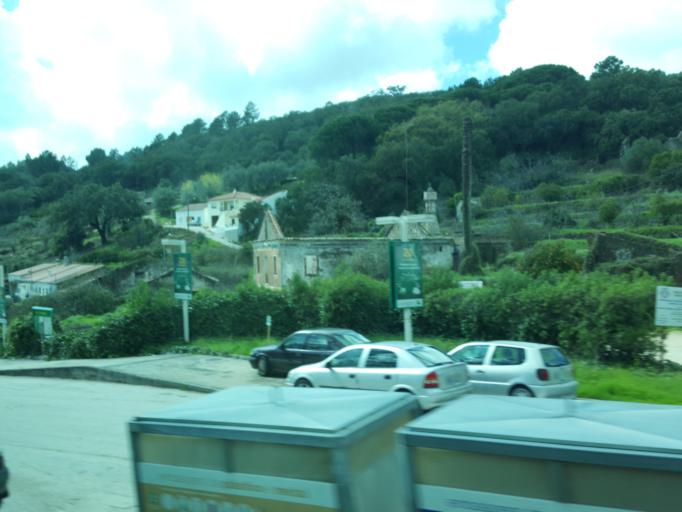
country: PT
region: Faro
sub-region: Monchique
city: Monchique
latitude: 37.3116
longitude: -8.5560
